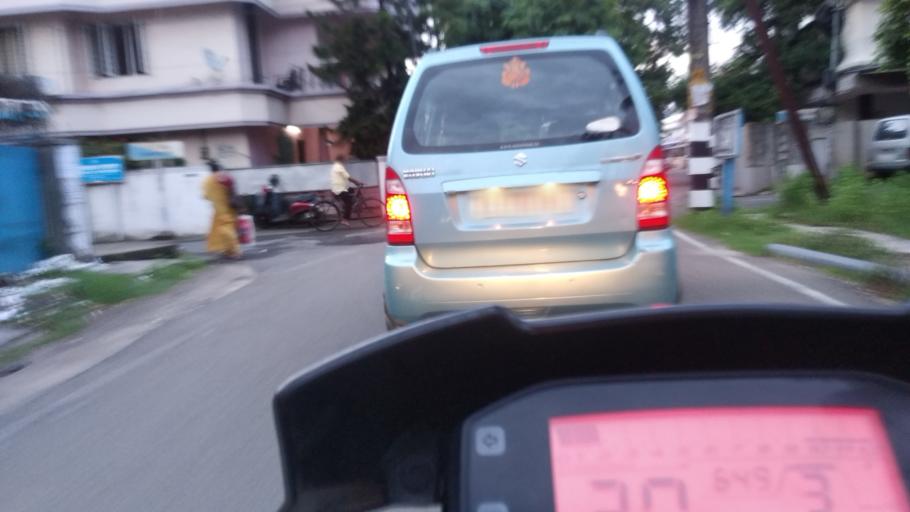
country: IN
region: Kerala
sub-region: Ernakulam
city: Elur
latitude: 10.0108
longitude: 76.2758
